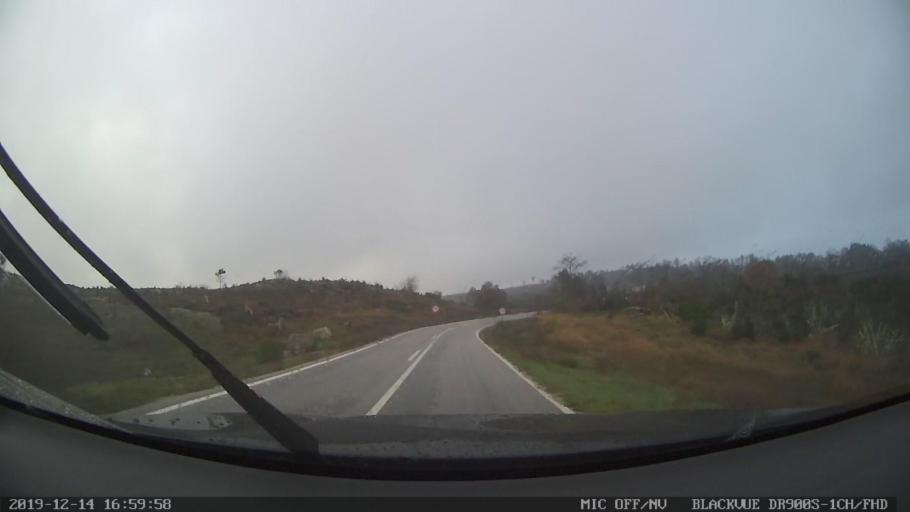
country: PT
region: Vila Real
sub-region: Vila Pouca de Aguiar
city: Vila Pouca de Aguiar
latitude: 41.4374
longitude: -7.5685
